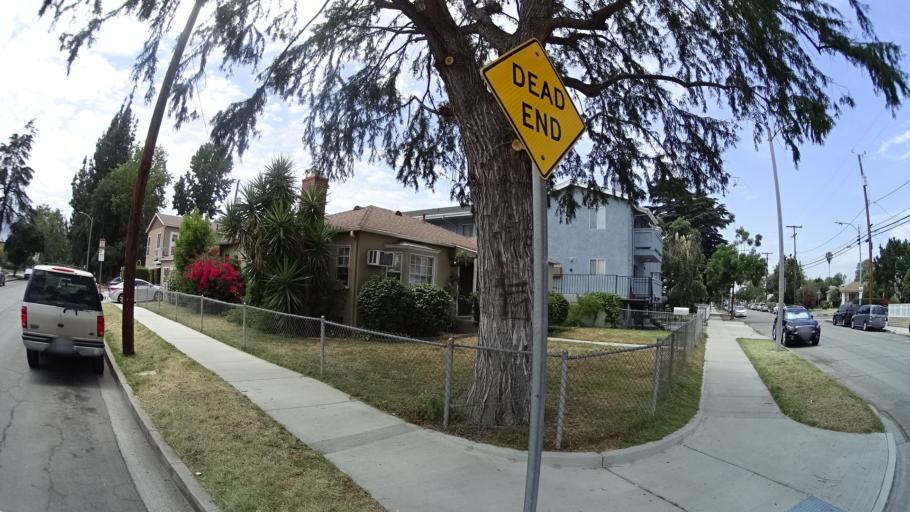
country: US
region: California
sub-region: Los Angeles County
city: Burbank
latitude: 34.1670
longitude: -118.3028
